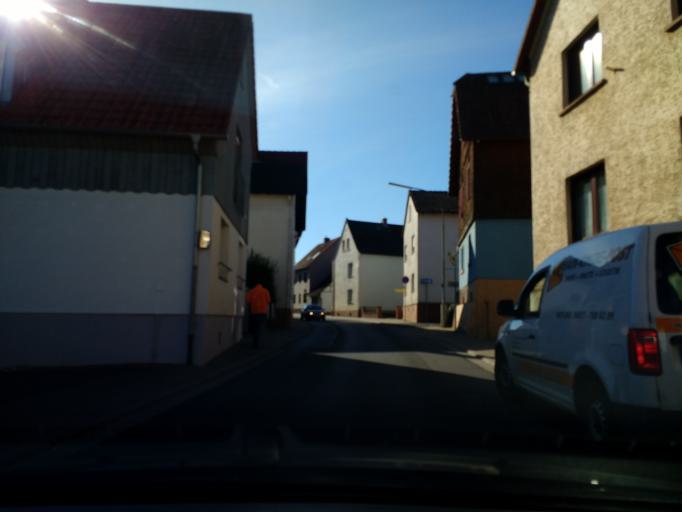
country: DE
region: Bavaria
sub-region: Regierungsbezirk Unterfranken
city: Geiselbach
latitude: 50.1418
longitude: 9.1429
